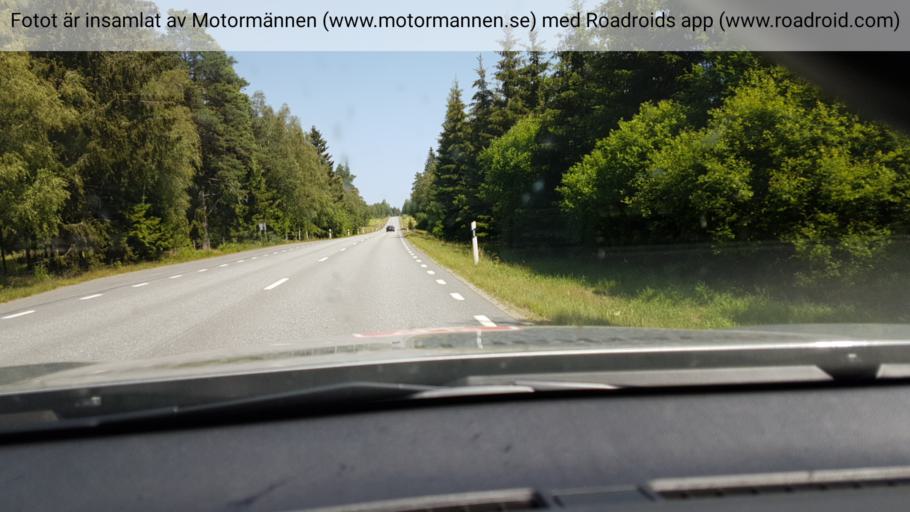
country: SE
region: Joenkoeping
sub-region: Nassjo Kommun
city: Bodafors
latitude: 57.4463
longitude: 14.7160
